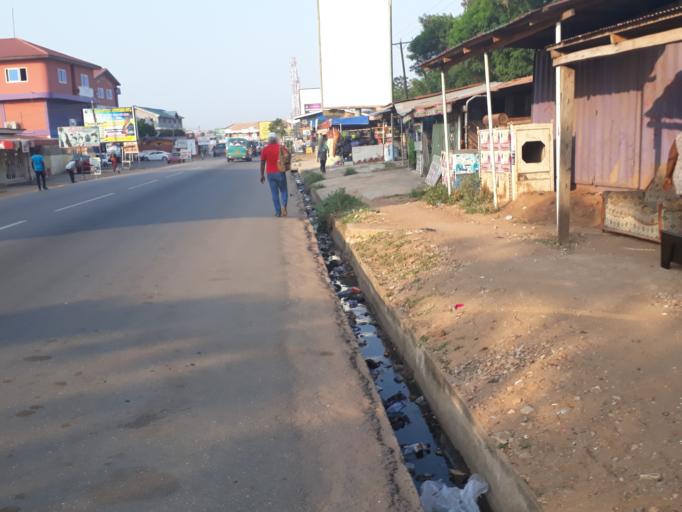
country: GH
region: Greater Accra
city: Dome
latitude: 5.6408
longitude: -0.2402
